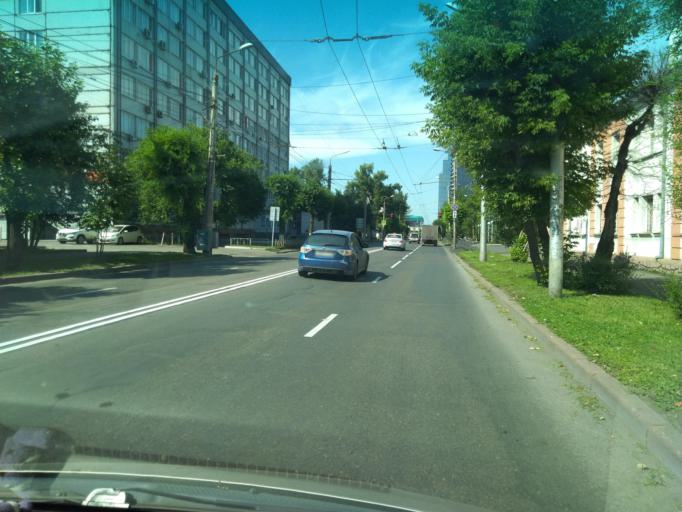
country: RU
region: Krasnoyarskiy
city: Krasnoyarsk
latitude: 56.0163
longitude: 92.8385
